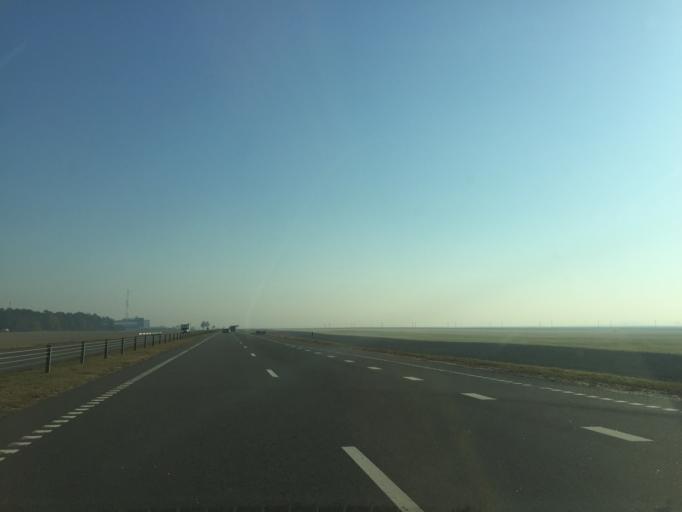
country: BY
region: Gomel
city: Kastsyukowka
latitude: 52.4925
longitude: 30.8379
